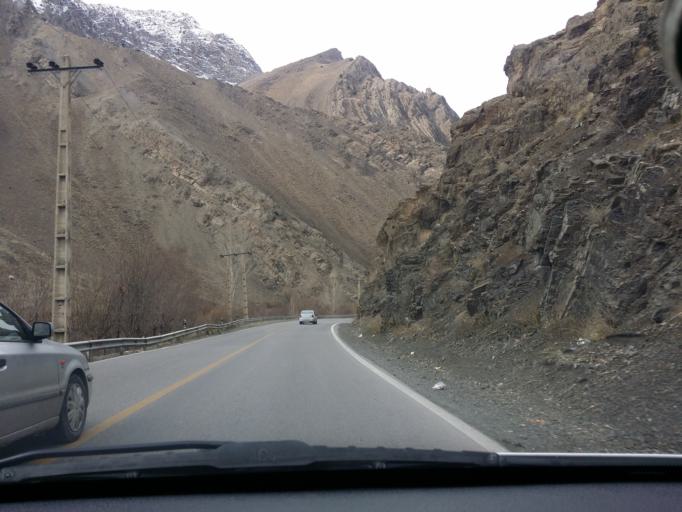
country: IR
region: Tehran
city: Tajrish
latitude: 36.0154
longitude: 51.2831
